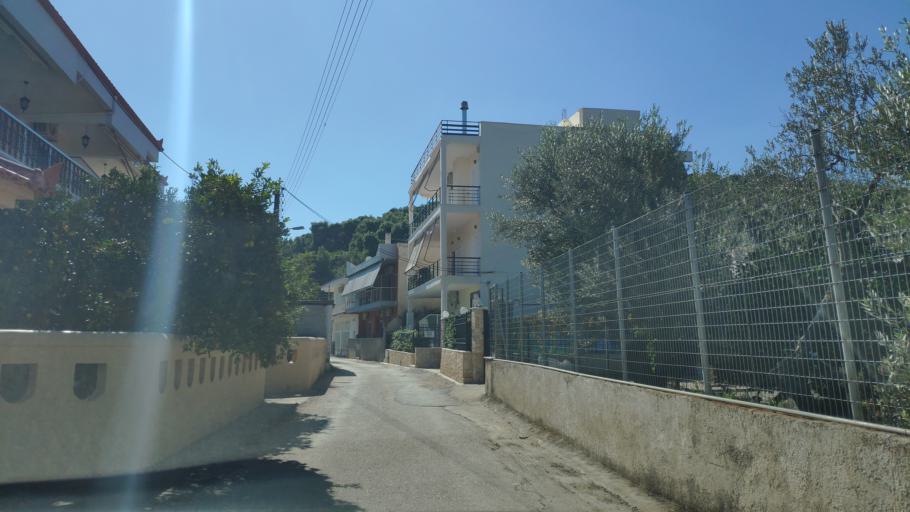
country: GR
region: Peloponnese
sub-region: Nomos Korinthias
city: Loutra Oraias Elenis
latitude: 37.8478
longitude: 22.9995
